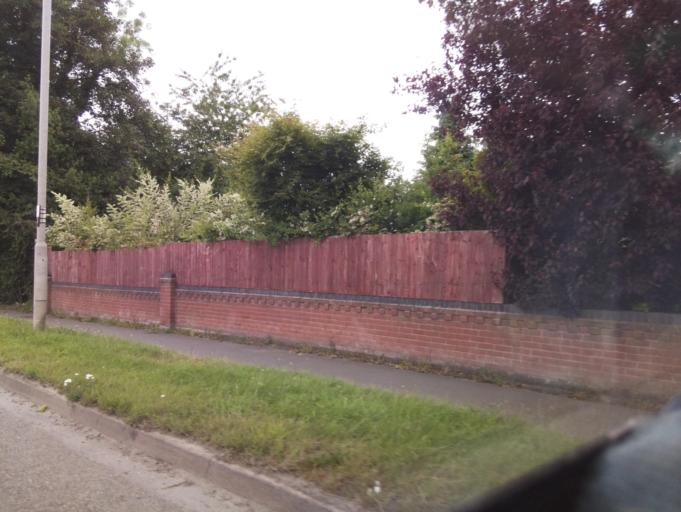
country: GB
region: England
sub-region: Leicestershire
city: Coalville
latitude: 52.7175
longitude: -1.3530
